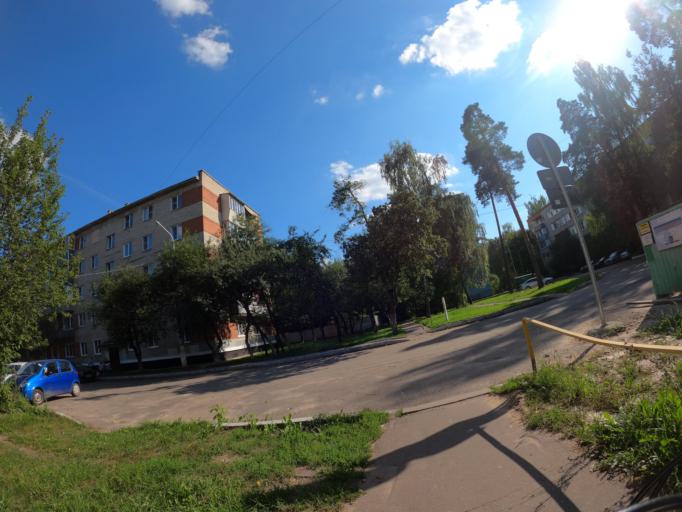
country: RU
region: Moskovskaya
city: Stupino
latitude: 54.8834
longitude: 38.0651
